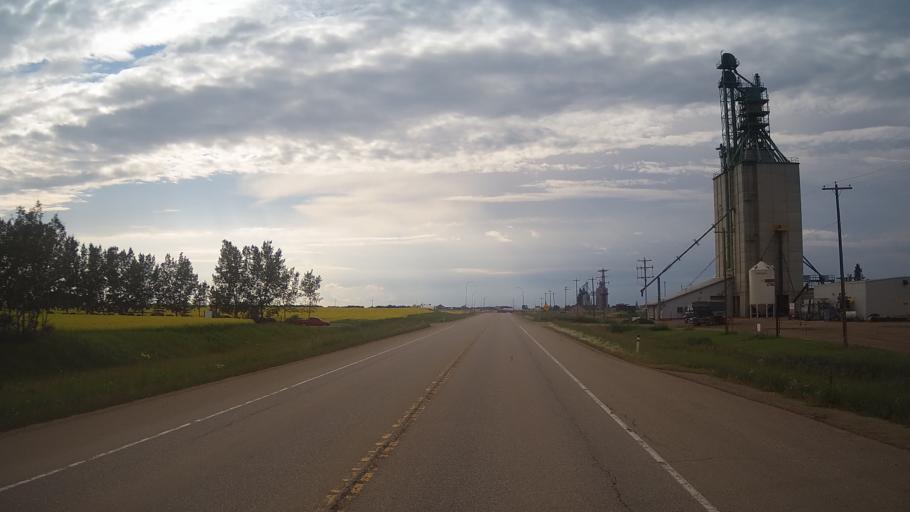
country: CA
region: Alberta
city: Viking
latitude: 53.0907
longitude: -111.7756
